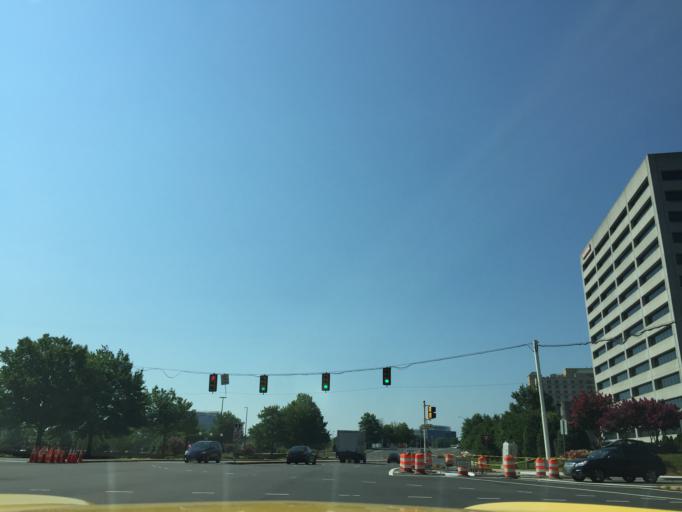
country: US
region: Virginia
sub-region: Fairfax County
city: Tysons Corner
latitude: 38.9236
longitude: -77.2267
